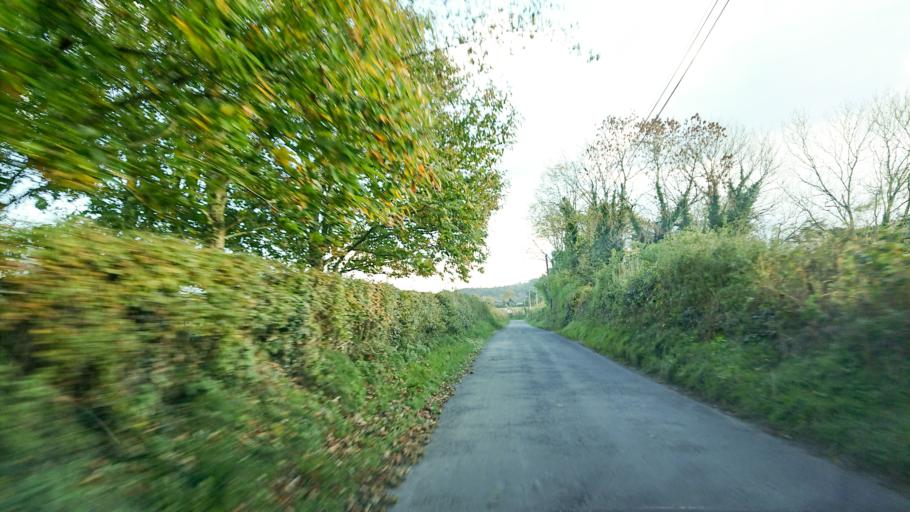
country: IE
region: Leinster
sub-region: Kilkenny
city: Graiguenamanagh
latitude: 52.4771
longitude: -6.9132
